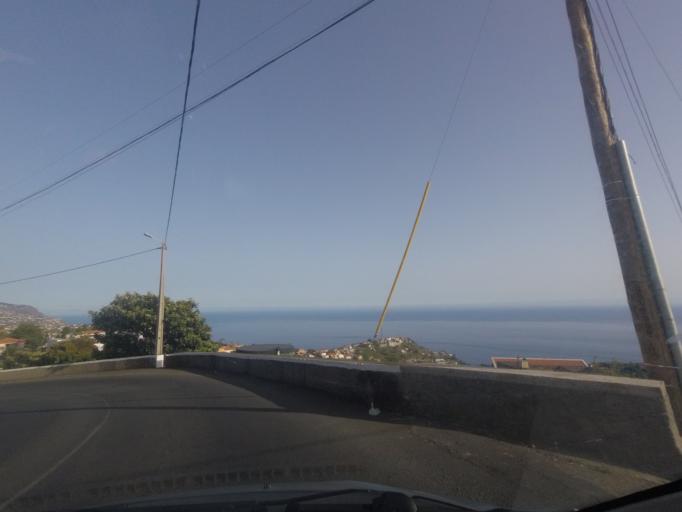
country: PT
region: Madeira
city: Ponta do Sol
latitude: 32.6961
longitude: -17.1133
